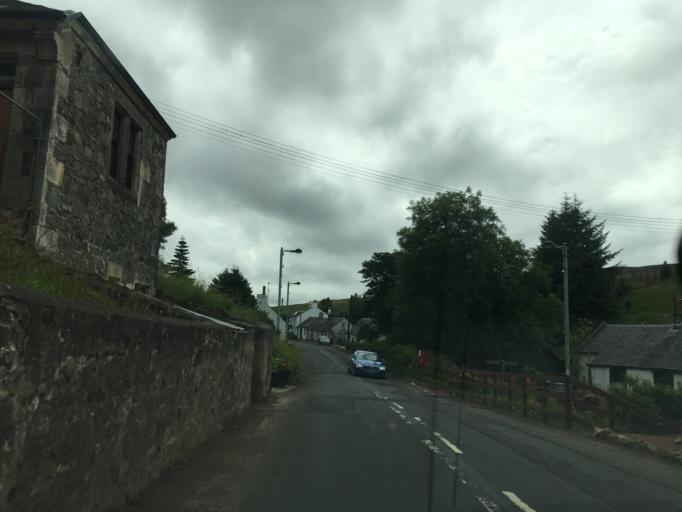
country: GB
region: Scotland
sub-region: South Lanarkshire
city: Douglas
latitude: 55.4141
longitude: -3.7625
